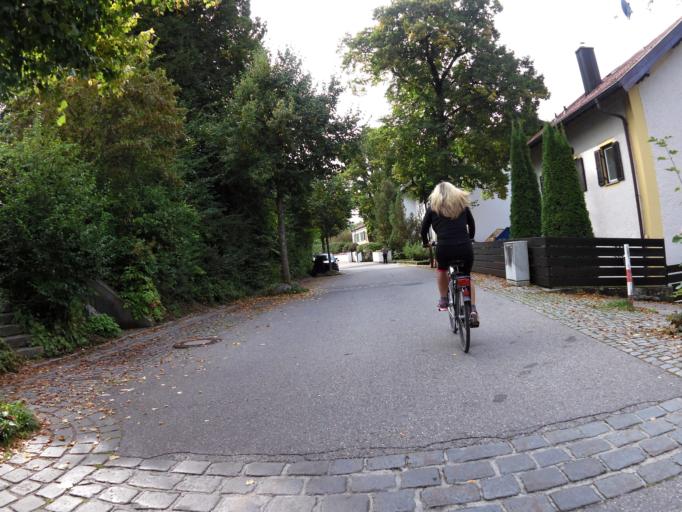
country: DE
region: Bavaria
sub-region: Upper Bavaria
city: Berg
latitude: 47.9719
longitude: 11.3511
